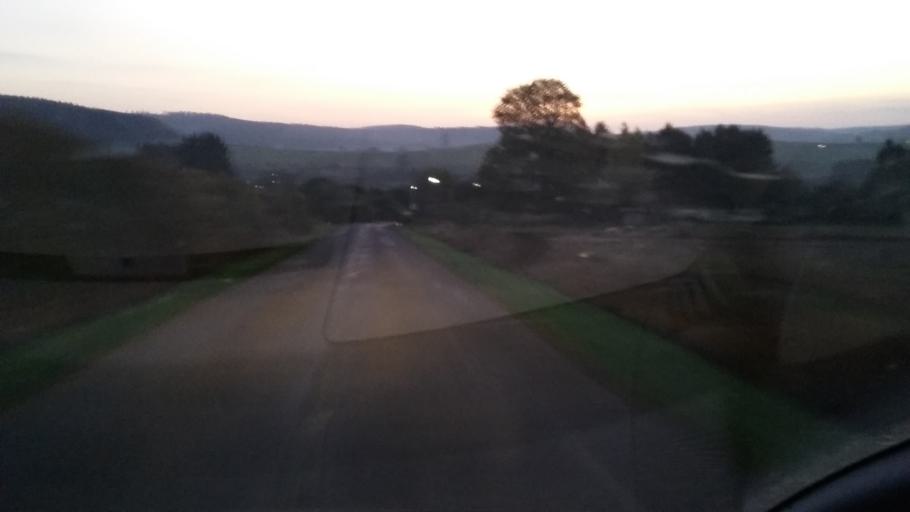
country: FR
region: Lorraine
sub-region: Departement de la Meuse
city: Montmedy
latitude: 49.5157
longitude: 5.3990
